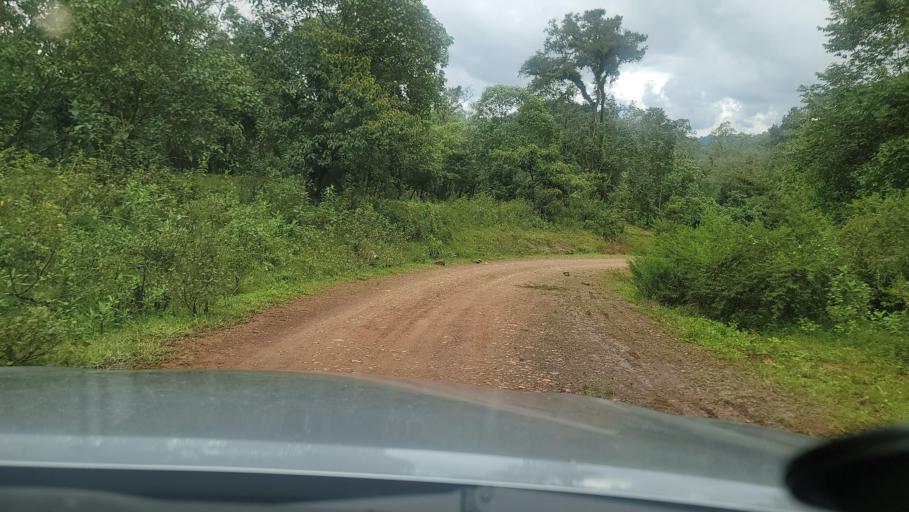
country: ET
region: Southern Nations, Nationalities, and People's Region
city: Bonga
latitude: 7.6220
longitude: 36.2103
